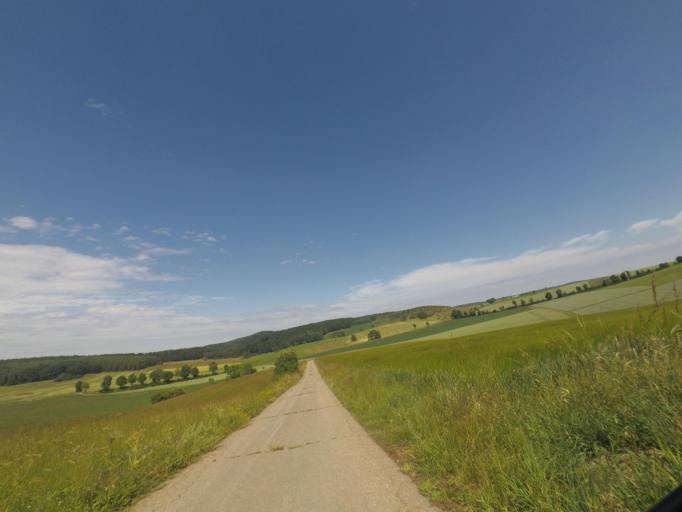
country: DE
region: Rheinland-Pfalz
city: Feusdorf
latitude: 50.3427
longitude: 6.6288
